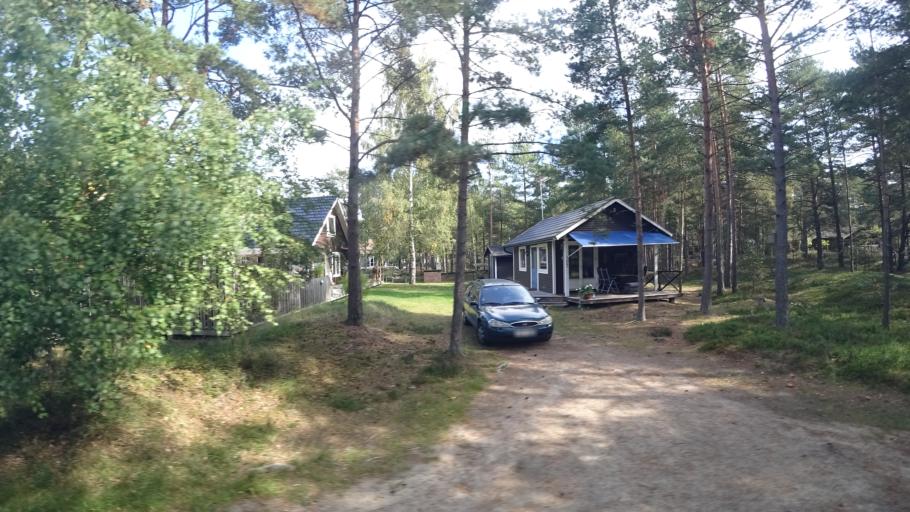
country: SE
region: Skane
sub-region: Kristianstads Kommun
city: Ahus
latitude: 55.9100
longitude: 14.2944
